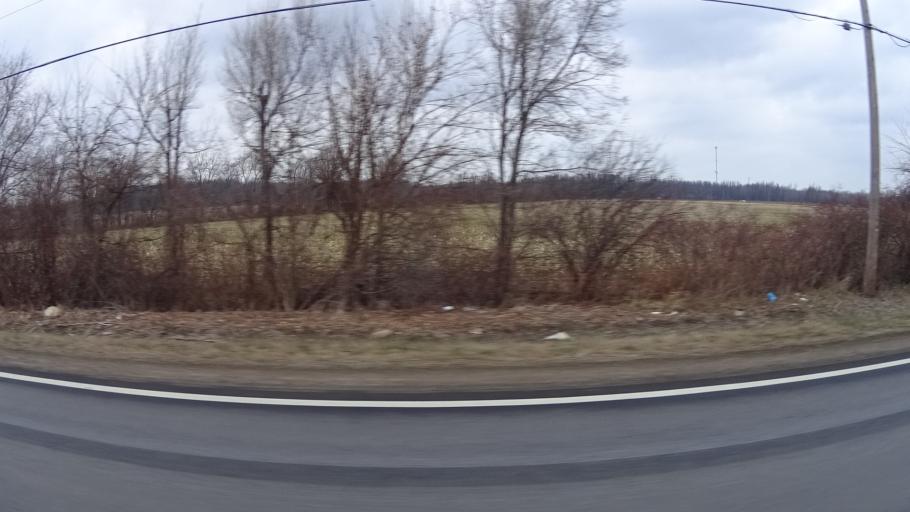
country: US
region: Ohio
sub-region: Lorain County
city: Amherst
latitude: 41.3705
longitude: -82.1743
